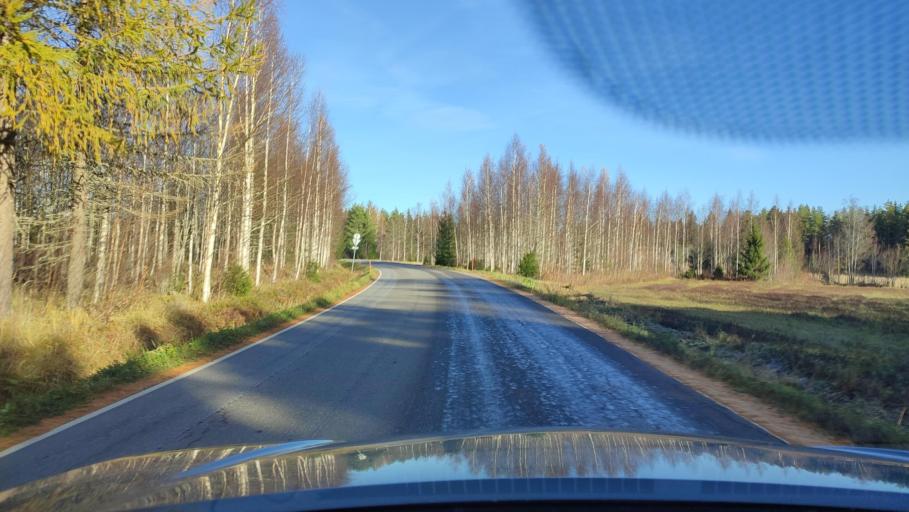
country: FI
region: Southern Ostrobothnia
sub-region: Suupohja
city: Karijoki
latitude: 62.3139
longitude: 21.7021
